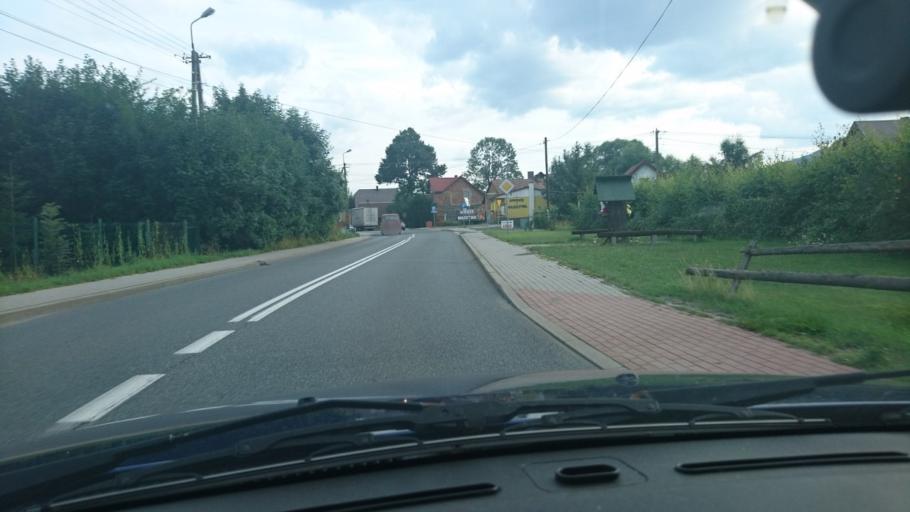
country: PL
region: Silesian Voivodeship
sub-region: Powiat zywiecki
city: Cisiec
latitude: 49.5950
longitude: 19.1072
